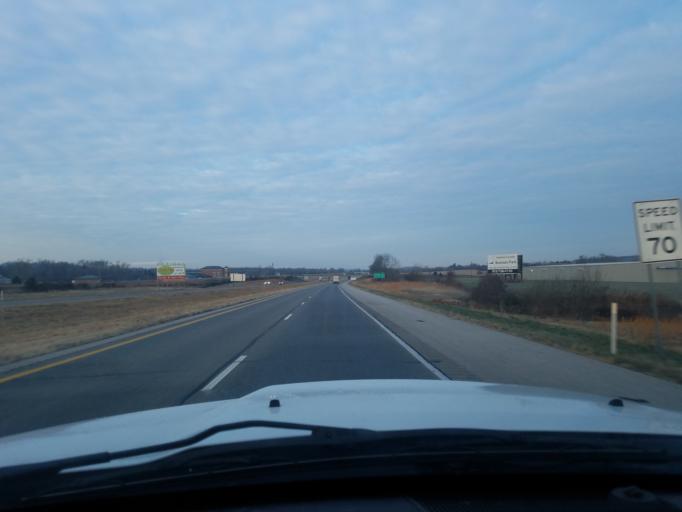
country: US
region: Indiana
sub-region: Harrison County
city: Corydon
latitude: 38.2393
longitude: -86.1392
